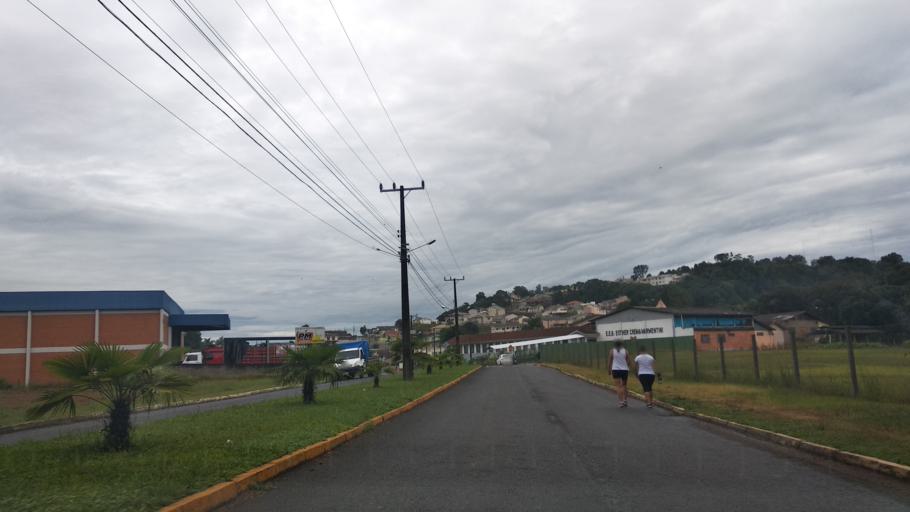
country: BR
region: Santa Catarina
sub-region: Videira
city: Videira
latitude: -26.9899
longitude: -51.1812
